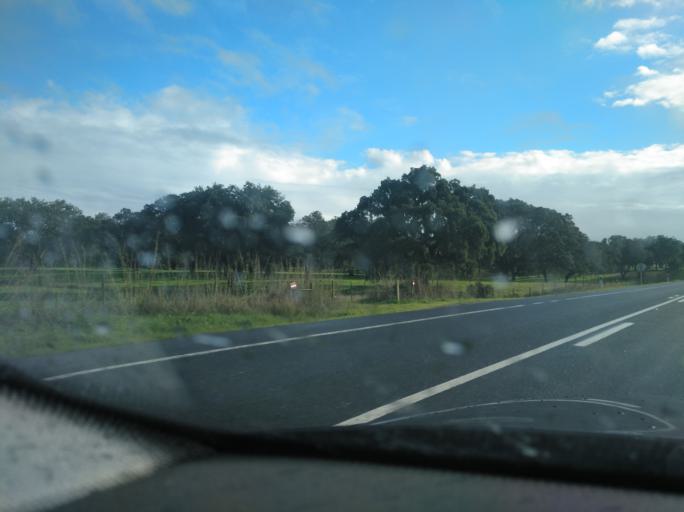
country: PT
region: Setubal
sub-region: Grandola
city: Grandola
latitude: 38.0424
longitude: -8.4013
